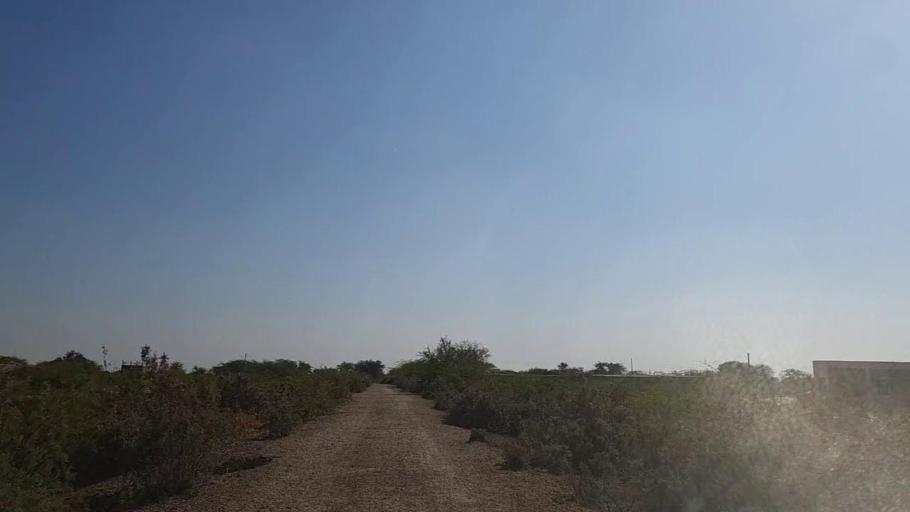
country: PK
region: Sindh
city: Samaro
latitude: 25.3980
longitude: 69.4317
